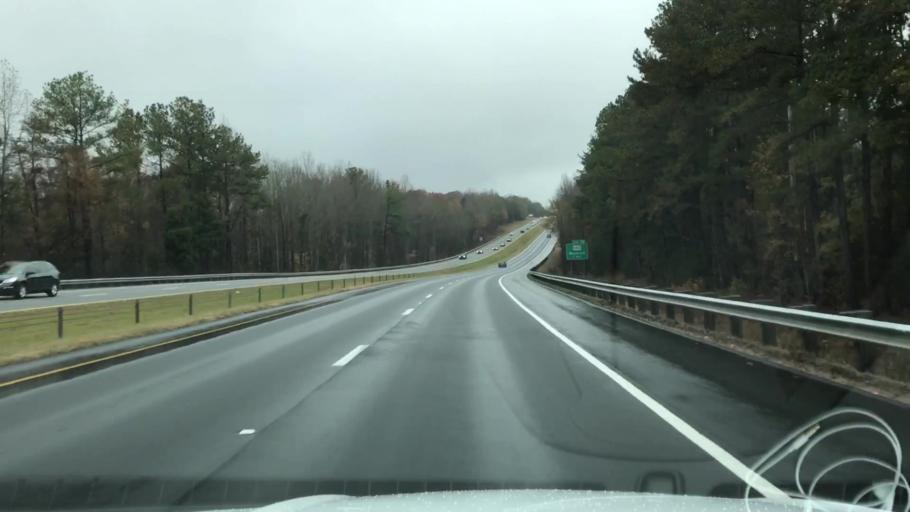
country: US
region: South Carolina
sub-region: Spartanburg County
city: Woodruff
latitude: 34.6797
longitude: -81.9379
